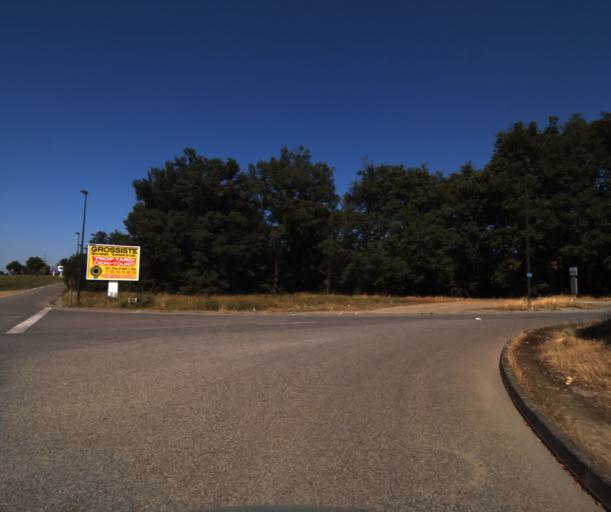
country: FR
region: Midi-Pyrenees
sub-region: Departement de la Haute-Garonne
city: Saubens
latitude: 43.4838
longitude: 1.3387
